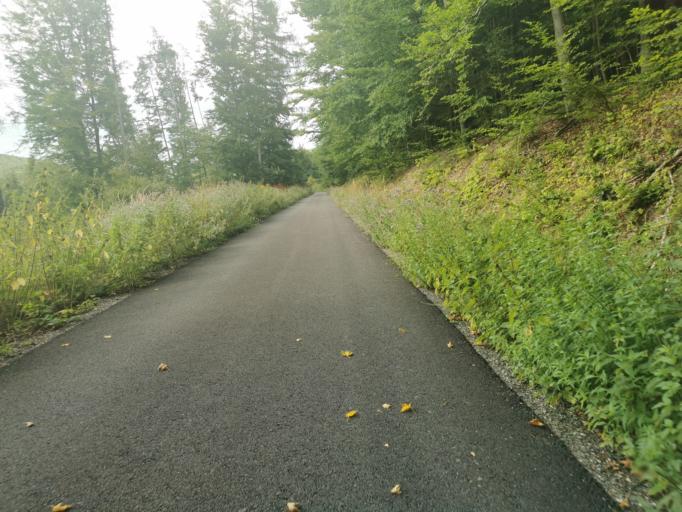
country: SK
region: Trenciansky
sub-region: Okres Myjava
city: Myjava
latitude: 48.8323
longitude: 17.6091
